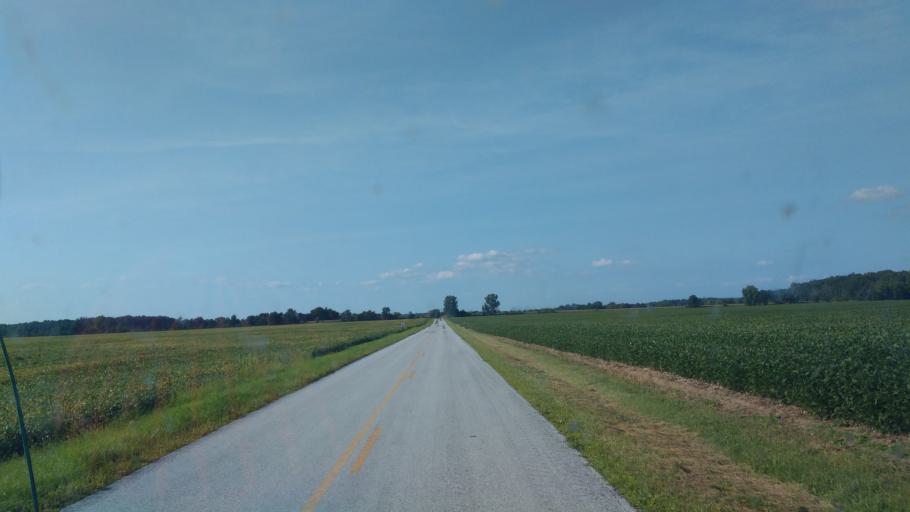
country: US
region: Ohio
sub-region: Hardin County
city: Kenton
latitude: 40.7247
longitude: -83.5727
